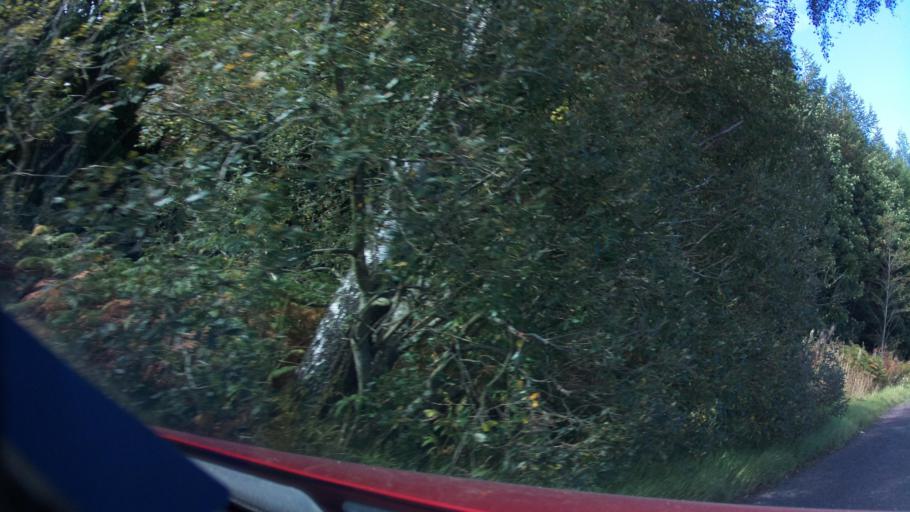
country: GB
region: Scotland
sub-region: South Lanarkshire
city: Biggar
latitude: 55.5480
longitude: -3.4125
